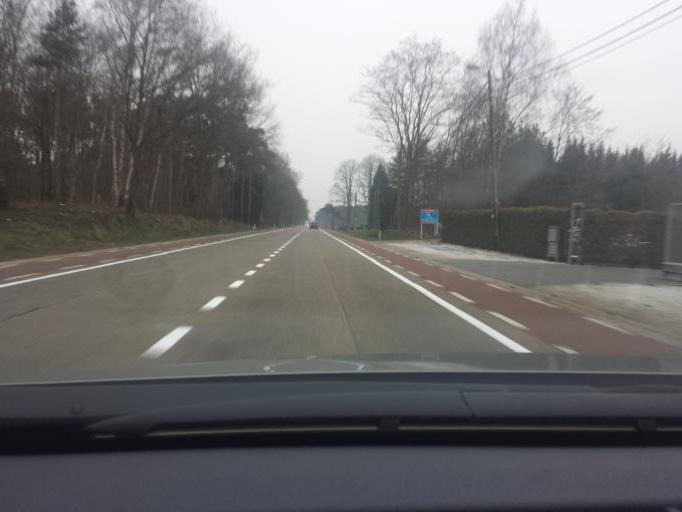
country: BE
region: Flanders
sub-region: Provincie Limburg
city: Lummen
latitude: 51.0266
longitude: 5.1517
